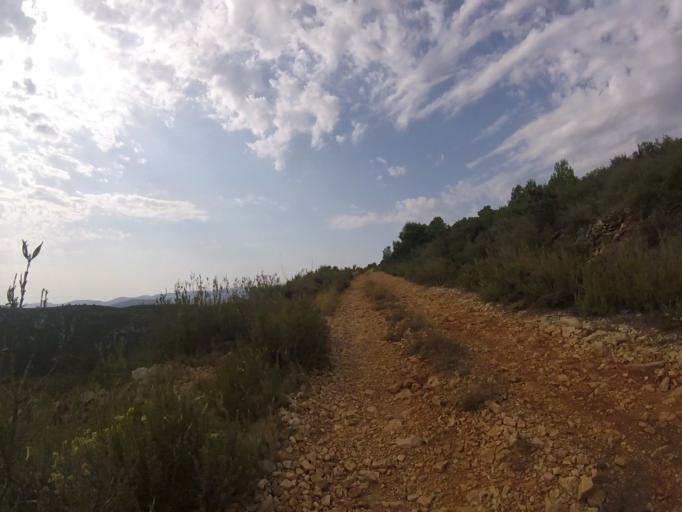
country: ES
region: Valencia
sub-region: Provincia de Castello
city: Alcala de Xivert
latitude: 40.3854
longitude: 0.2119
